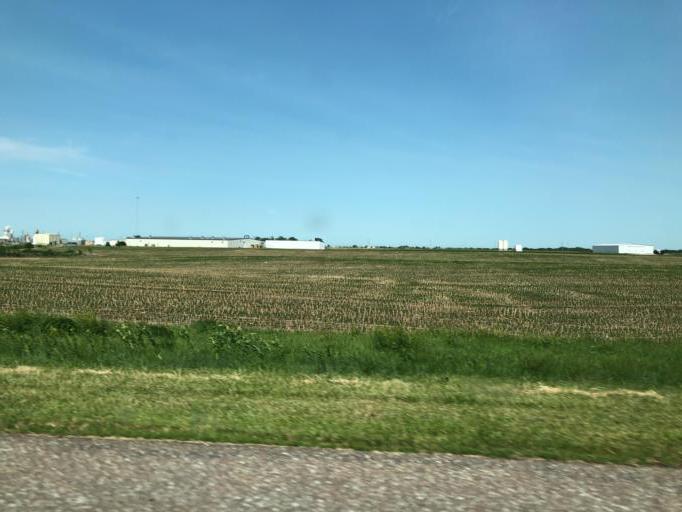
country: US
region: Nebraska
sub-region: Fillmore County
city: Geneva
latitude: 40.5361
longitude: -97.5867
